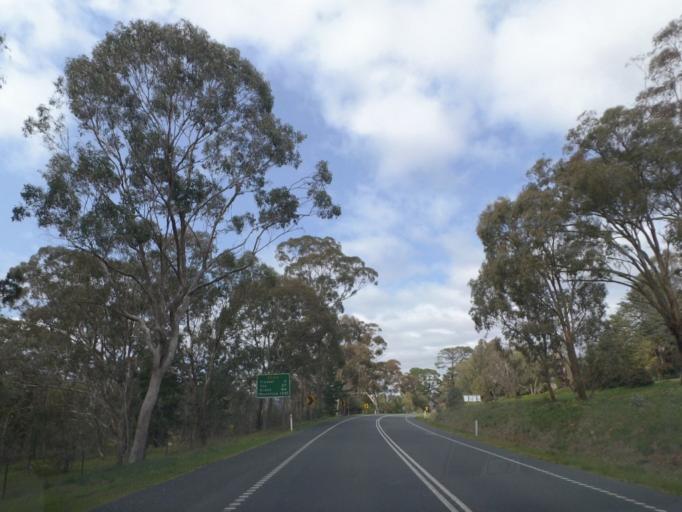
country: AU
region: Victoria
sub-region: Murrindindi
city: Kinglake West
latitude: -37.0964
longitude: 145.2071
